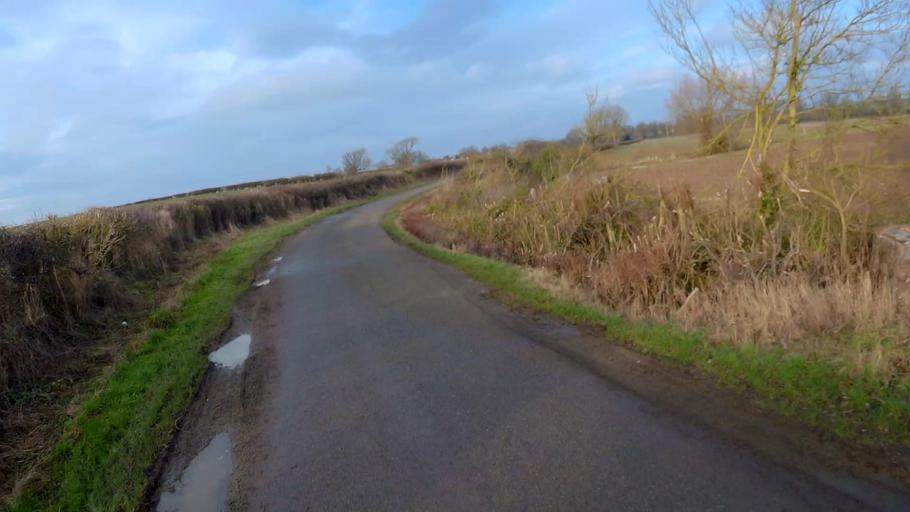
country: GB
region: England
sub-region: Lincolnshire
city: Bourne
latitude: 52.7727
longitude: -0.4256
